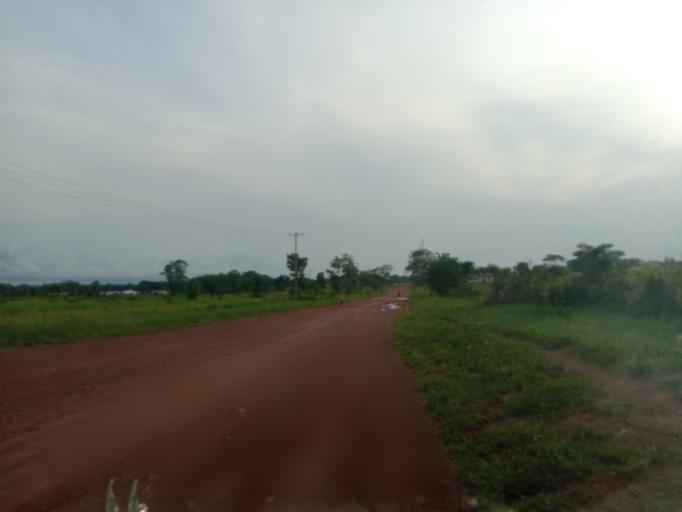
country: SL
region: Southern Province
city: Largo
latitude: 8.1144
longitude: -12.0646
